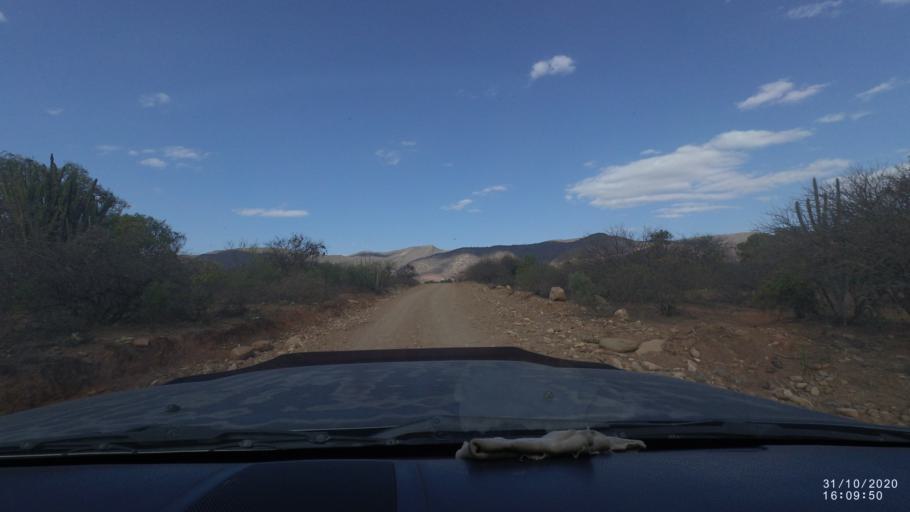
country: BO
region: Chuquisaca
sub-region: Provincia Zudanez
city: Mojocoya
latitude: -18.3849
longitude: -64.6348
